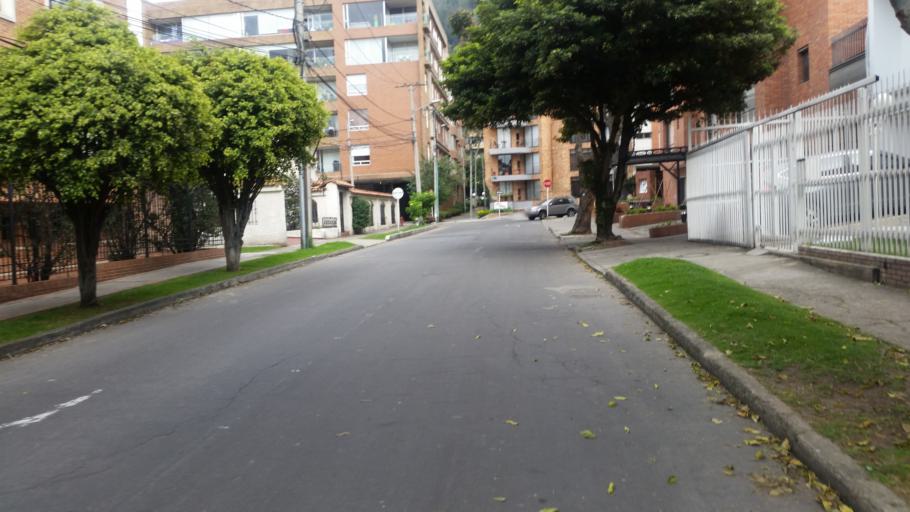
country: CO
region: Bogota D.C.
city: Barrio San Luis
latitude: 4.6781
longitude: -74.0430
